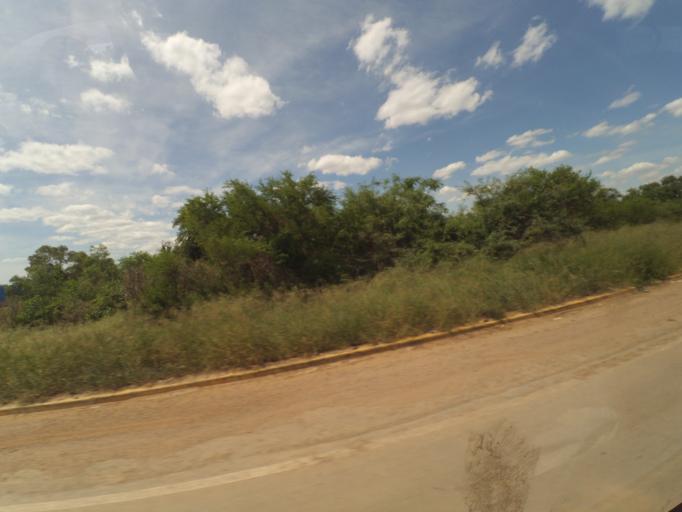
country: BO
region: Santa Cruz
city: Pailon
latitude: -17.5922
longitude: -61.9896
